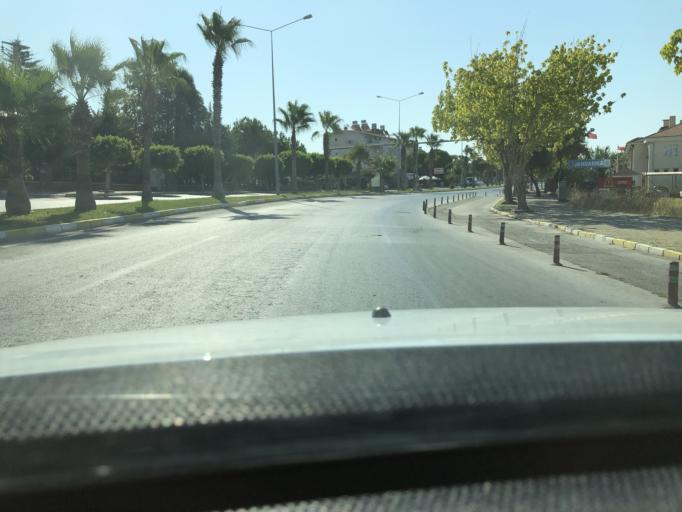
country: TR
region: Antalya
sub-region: Manavgat
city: Side
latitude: 36.7813
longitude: 31.3929
